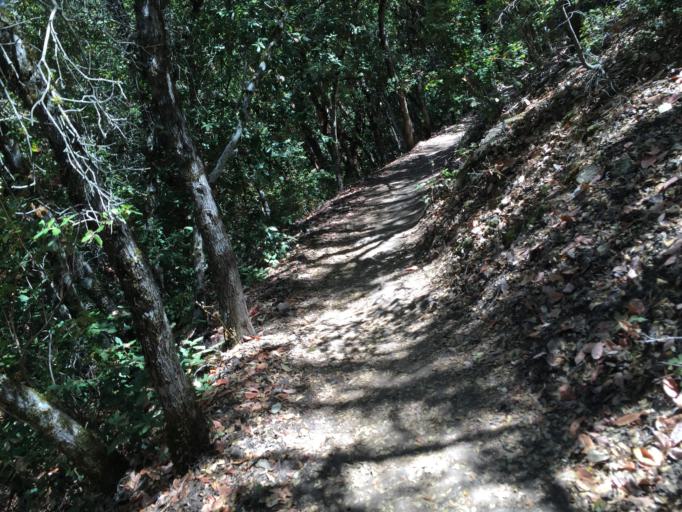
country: US
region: California
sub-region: Santa Clara County
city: Saratoga
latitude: 37.2305
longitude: -122.1140
